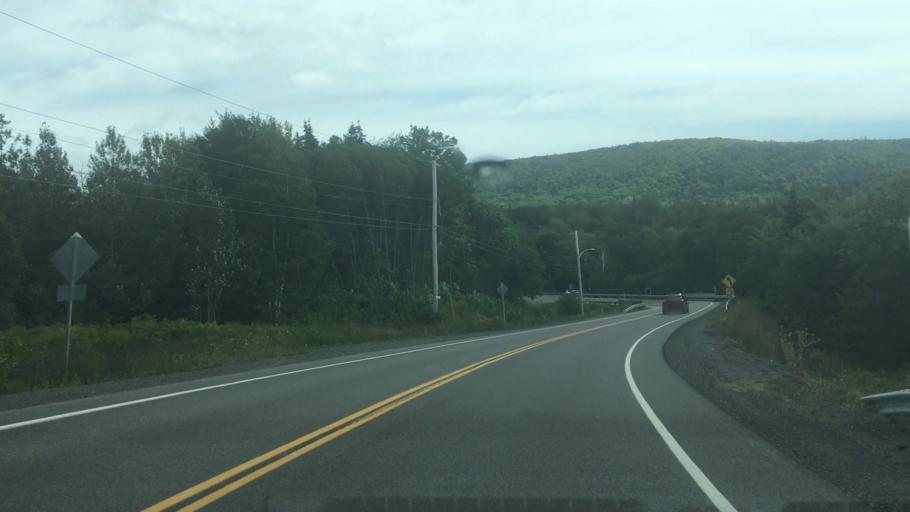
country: CA
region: Nova Scotia
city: Sydney Mines
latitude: 46.3082
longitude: -60.6207
